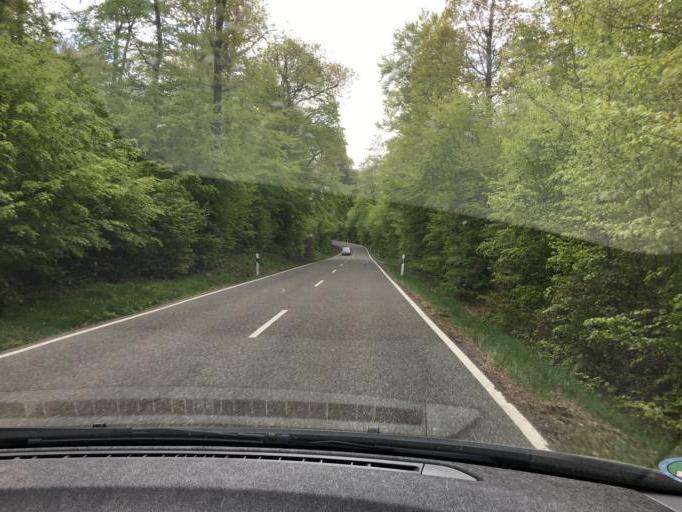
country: DE
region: North Rhine-Westphalia
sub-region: Regierungsbezirk Koln
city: Bad Munstereifel
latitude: 50.5462
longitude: 6.8156
